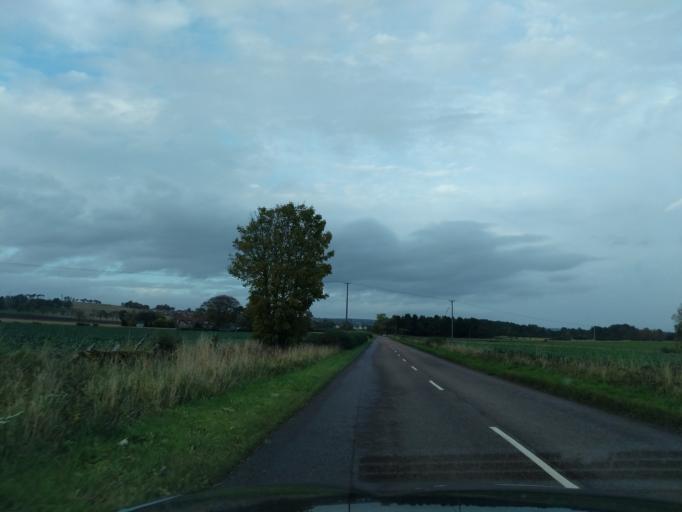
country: GB
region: Scotland
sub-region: Fife
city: Tayport
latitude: 56.4322
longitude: -2.8858
